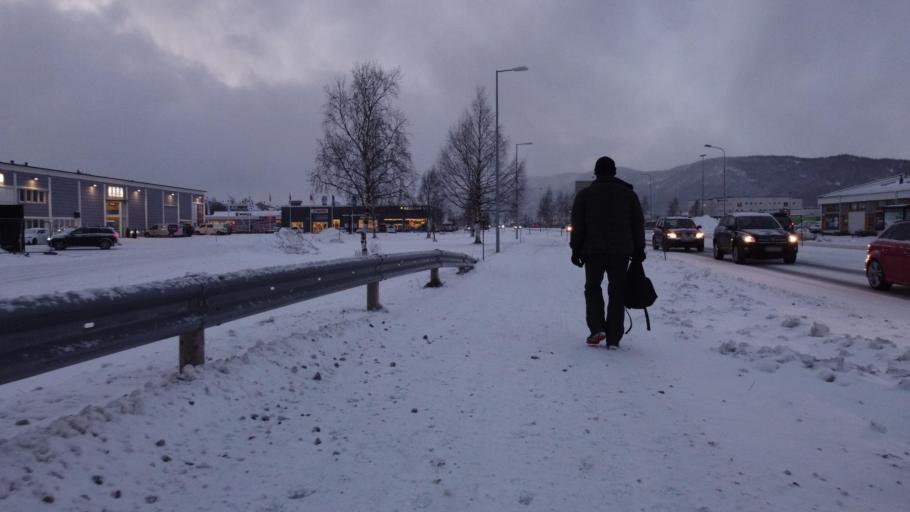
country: NO
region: Nordland
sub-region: Rana
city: Mo i Rana
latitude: 66.3184
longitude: 14.1484
